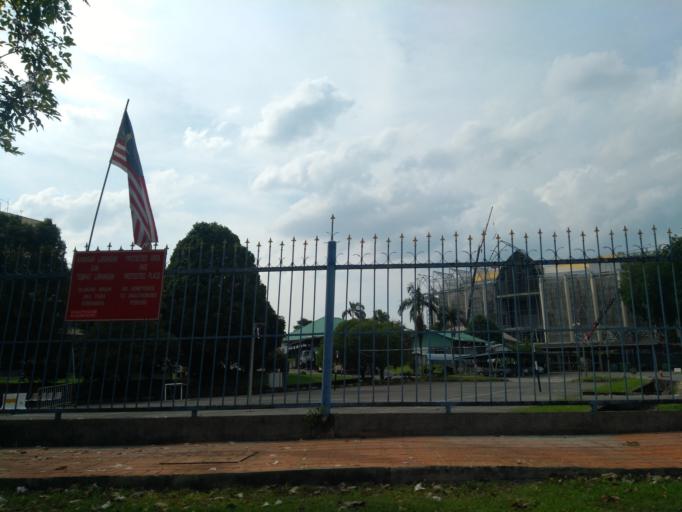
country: MY
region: Sarawak
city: Kuching
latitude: 1.5534
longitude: 110.3421
